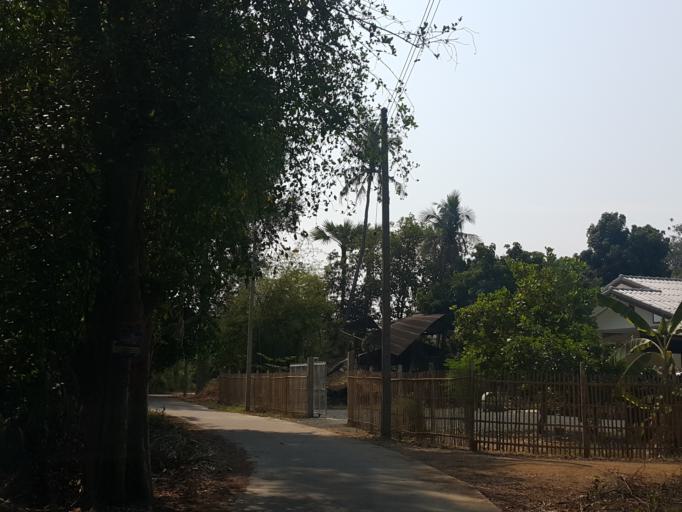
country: TH
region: Chiang Mai
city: San Kamphaeng
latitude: 18.7551
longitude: 99.1389
